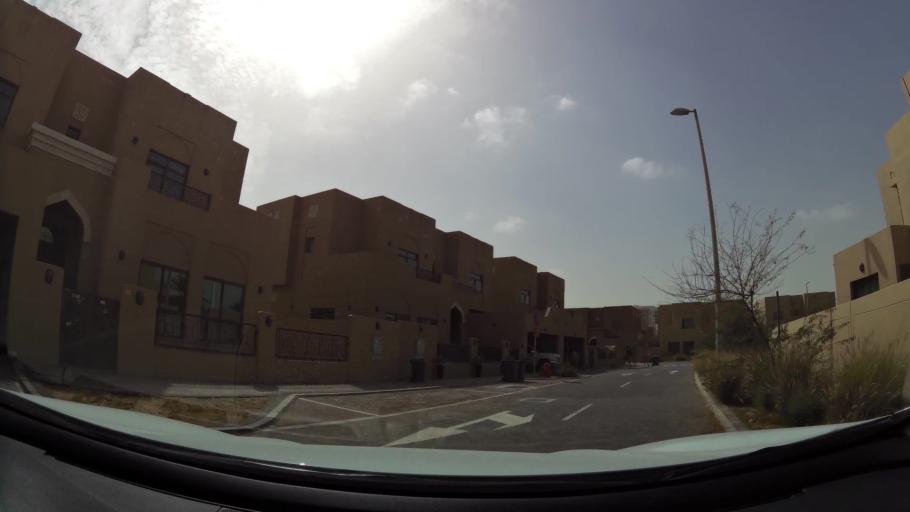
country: AE
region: Abu Dhabi
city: Abu Dhabi
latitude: 24.4138
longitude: 54.5405
